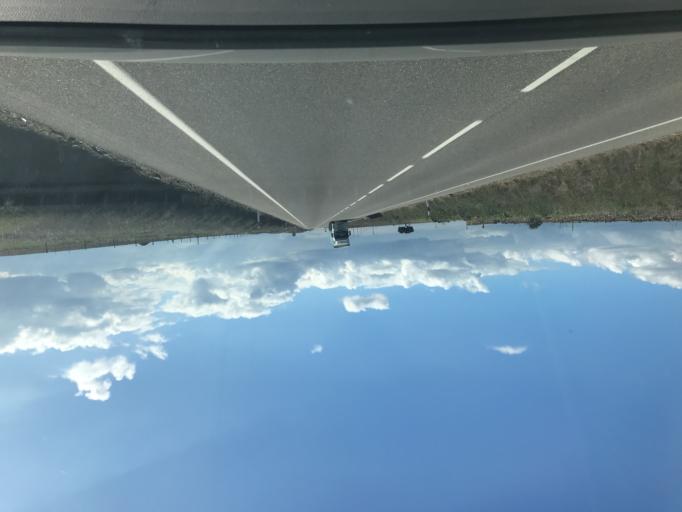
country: ES
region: Extremadura
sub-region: Provincia de Badajoz
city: Granja de Torrehermosa
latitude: 38.2816
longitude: -5.5187
